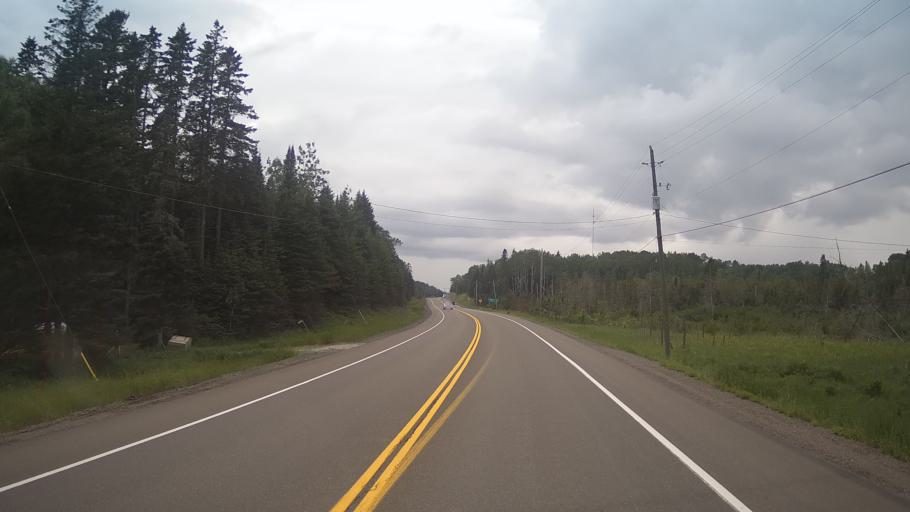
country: CA
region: Ontario
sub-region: Thunder Bay District
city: Thunder Bay
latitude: 48.5055
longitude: -89.4501
